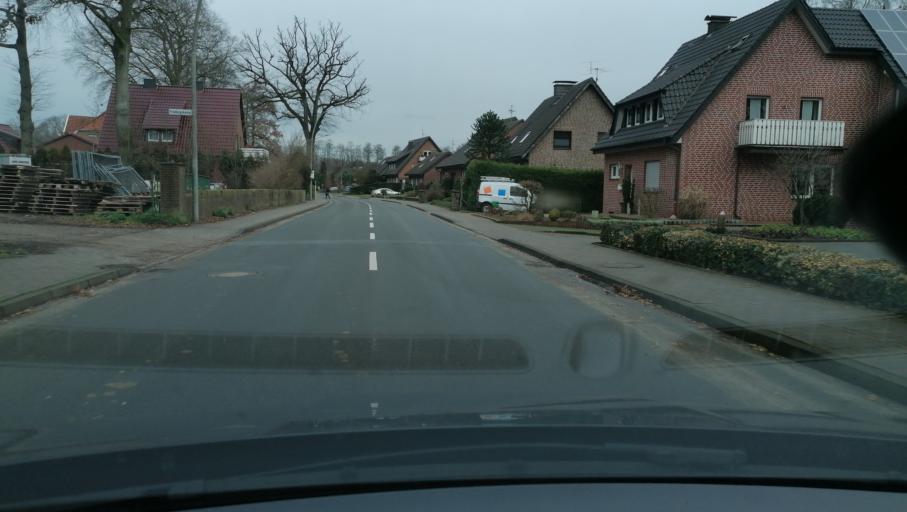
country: DE
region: North Rhine-Westphalia
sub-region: Regierungsbezirk Munster
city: Klein Reken
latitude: 51.7879
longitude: 7.0386
